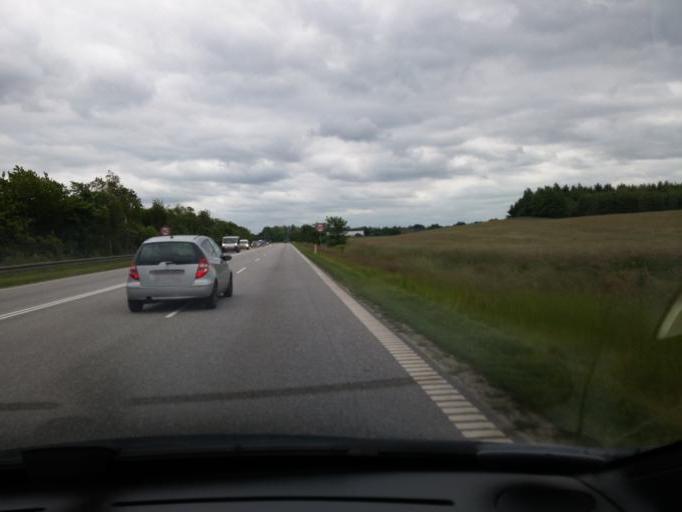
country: DK
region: Capital Region
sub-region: Allerod Kommune
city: Lillerod
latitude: 55.8558
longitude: 12.3232
